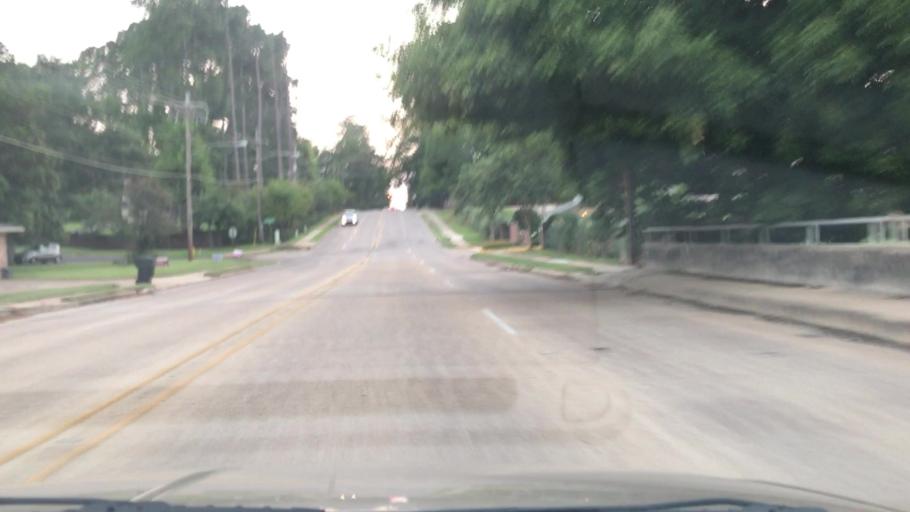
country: US
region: Louisiana
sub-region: Bossier Parish
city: Bossier City
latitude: 32.4547
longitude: -93.7346
